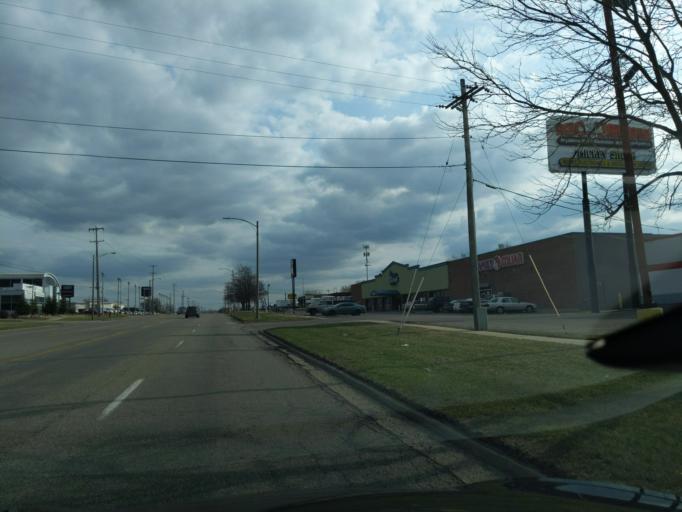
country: US
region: Michigan
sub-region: Ingham County
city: Holt
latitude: 42.6739
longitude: -84.5383
